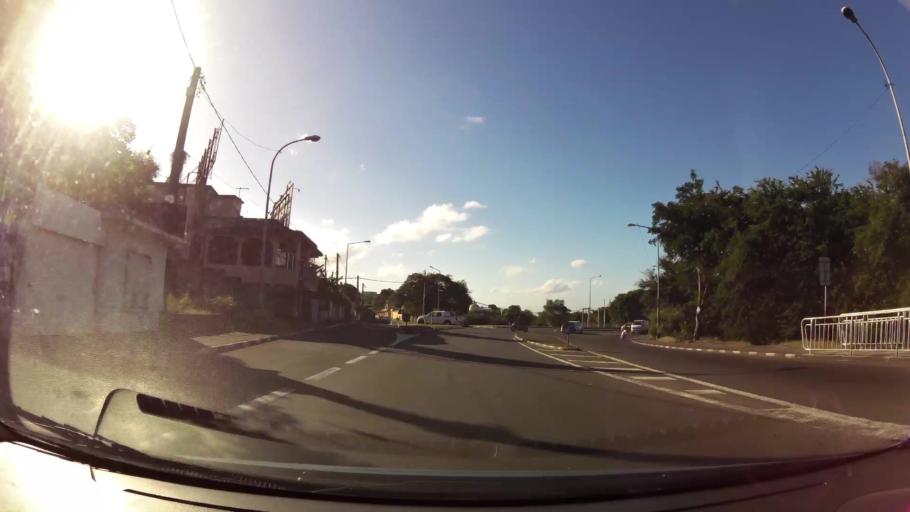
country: MU
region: Moka
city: Pailles
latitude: -20.1761
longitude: 57.4711
